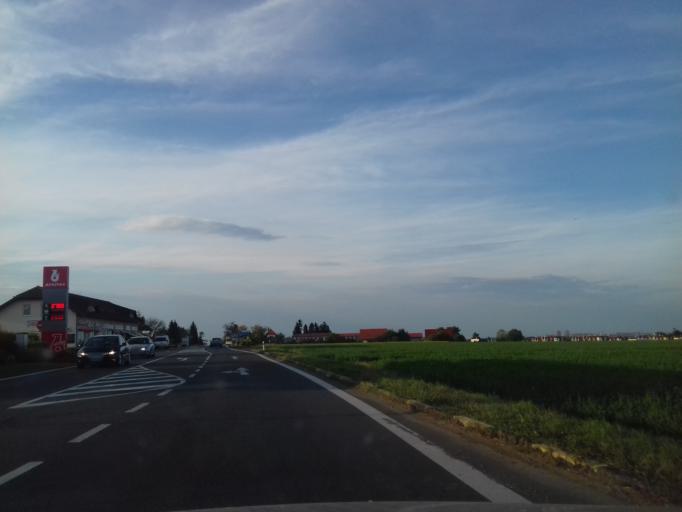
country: CZ
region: Central Bohemia
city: Vestec
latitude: 49.9728
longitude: 14.5030
